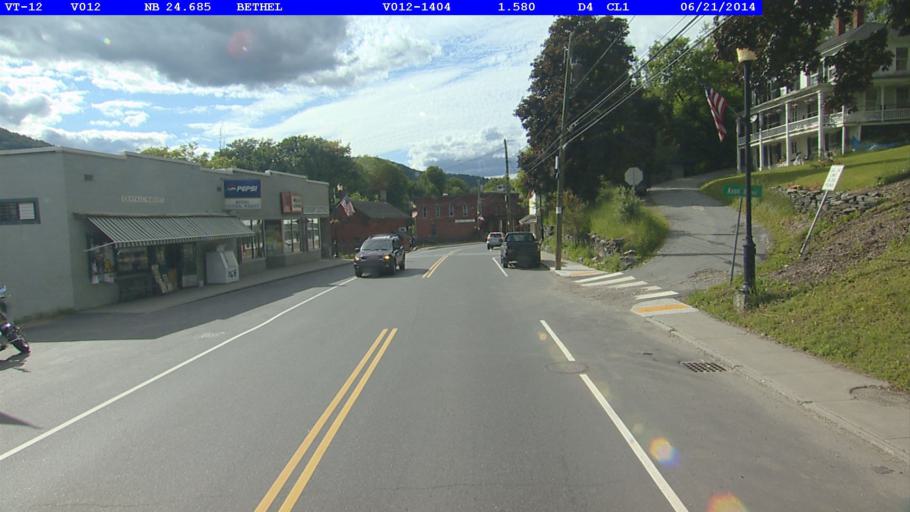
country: US
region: Vermont
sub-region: Orange County
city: Randolph
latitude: 43.8305
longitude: -72.6327
